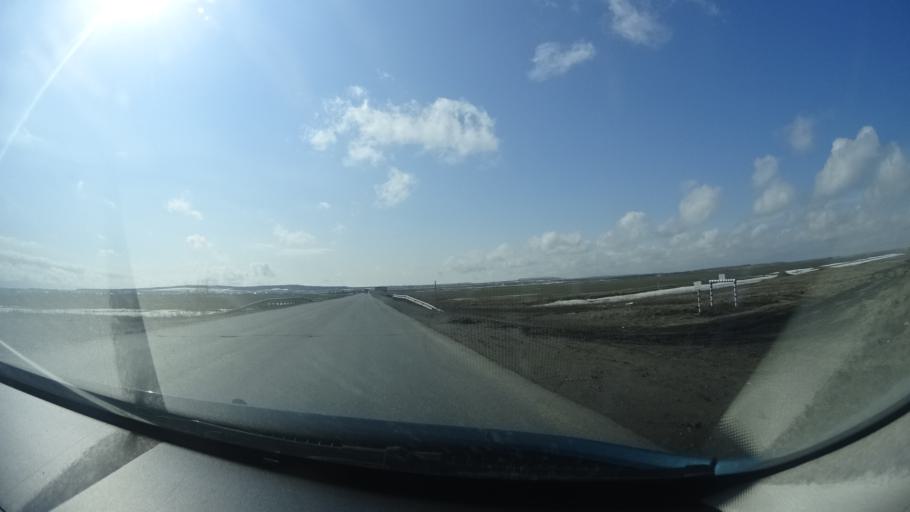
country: RU
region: Bashkortostan
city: Mikhaylovka
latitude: 54.8919
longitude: 55.7208
